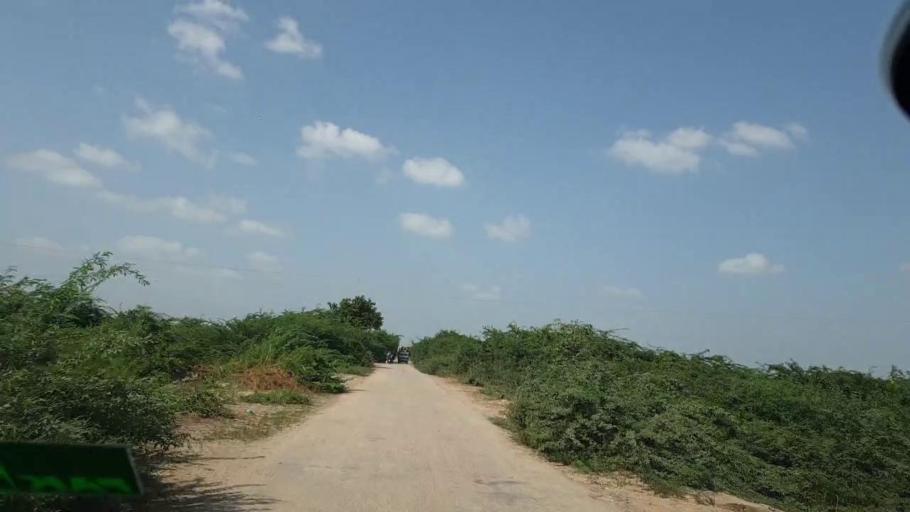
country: PK
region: Sindh
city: Naukot
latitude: 24.6387
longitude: 69.2273
